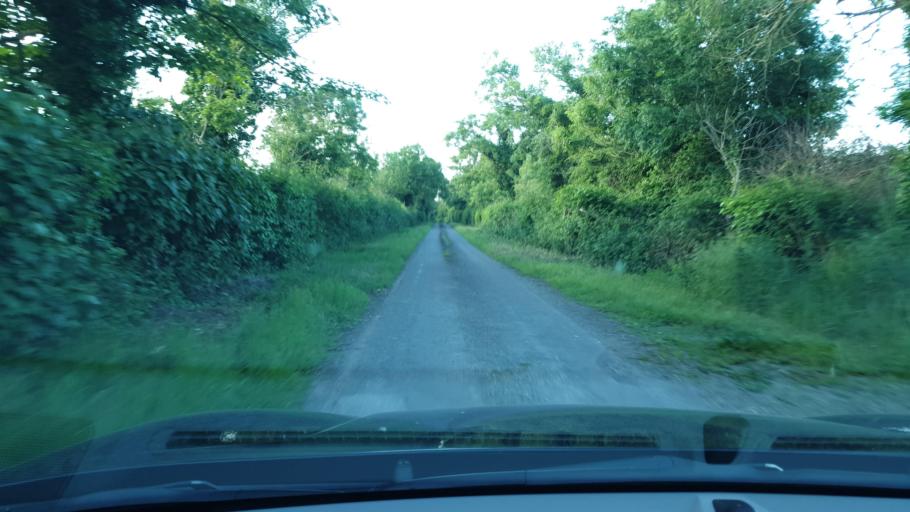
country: IE
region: Leinster
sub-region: An Mhi
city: Ashbourne
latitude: 53.4564
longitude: -6.4086
